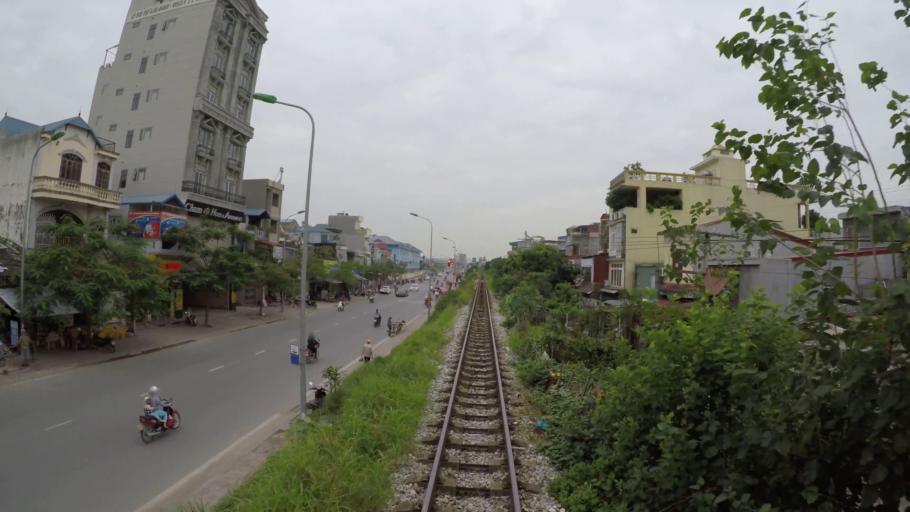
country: VN
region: Hai Phong
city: An Duong
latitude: 20.8728
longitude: 106.6458
